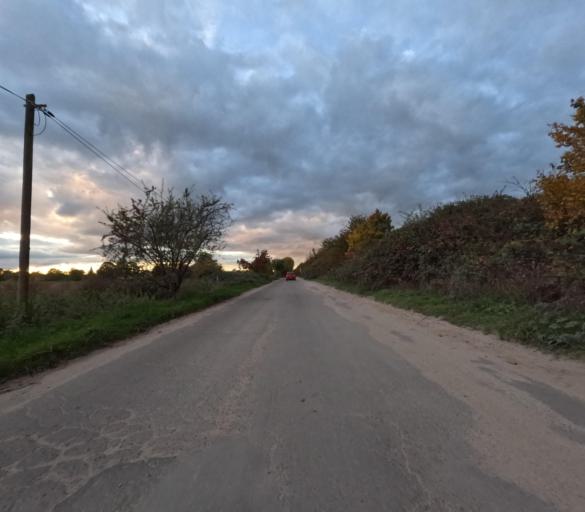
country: DE
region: Saxony
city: Borsdorf
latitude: 51.3098
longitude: 12.5275
